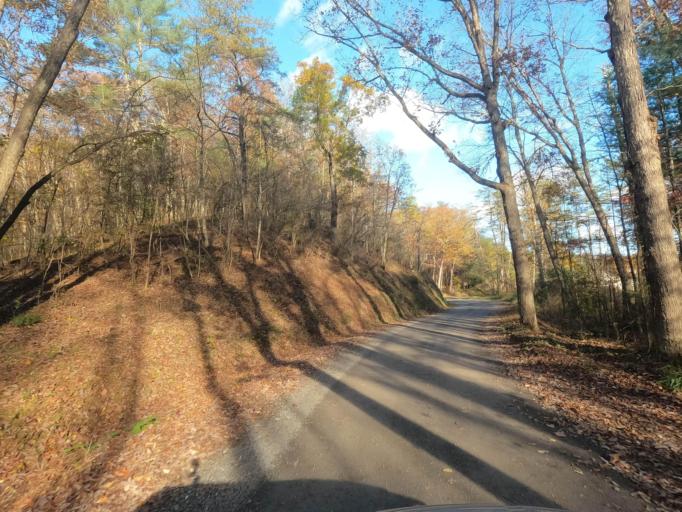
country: US
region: West Virginia
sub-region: Morgan County
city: Berkeley Springs
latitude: 39.6715
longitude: -78.4594
